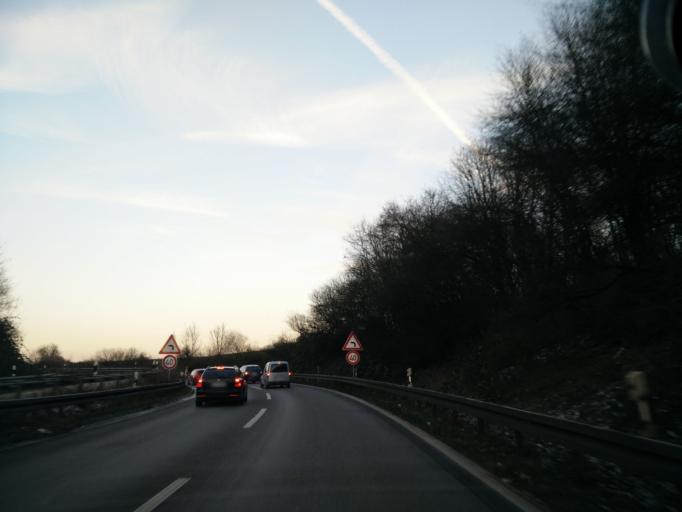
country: DE
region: North Rhine-Westphalia
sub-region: Regierungsbezirk Dusseldorf
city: Ratingen
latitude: 51.2974
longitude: 6.8988
